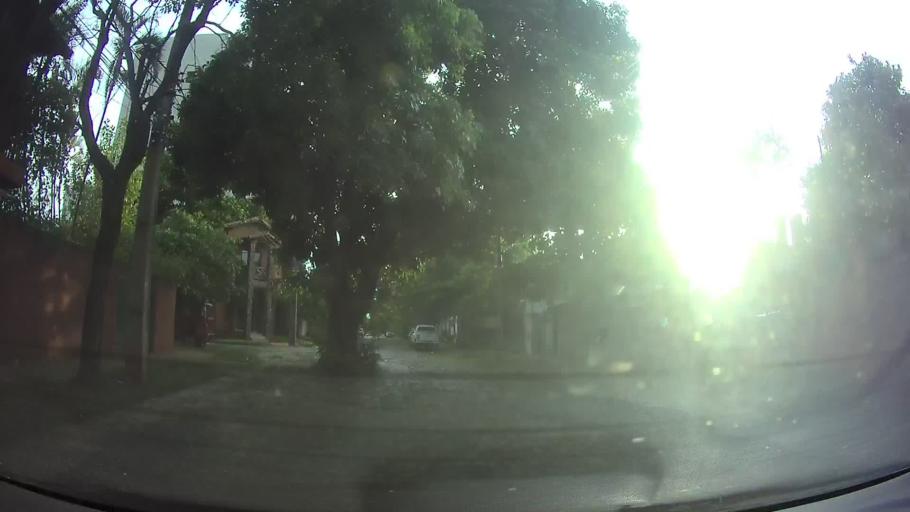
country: PY
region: Asuncion
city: Asuncion
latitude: -25.2755
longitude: -57.5705
